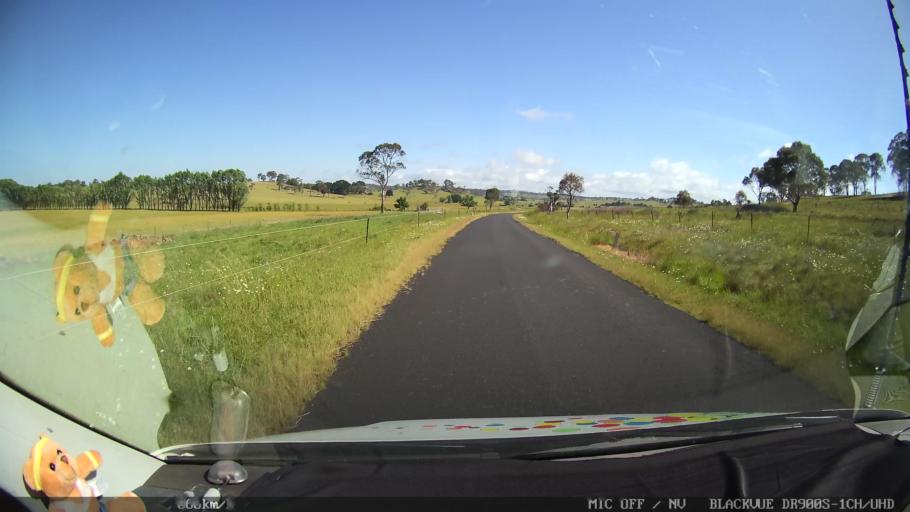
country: AU
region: New South Wales
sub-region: Guyra
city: Guyra
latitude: -30.1553
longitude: 151.6809
